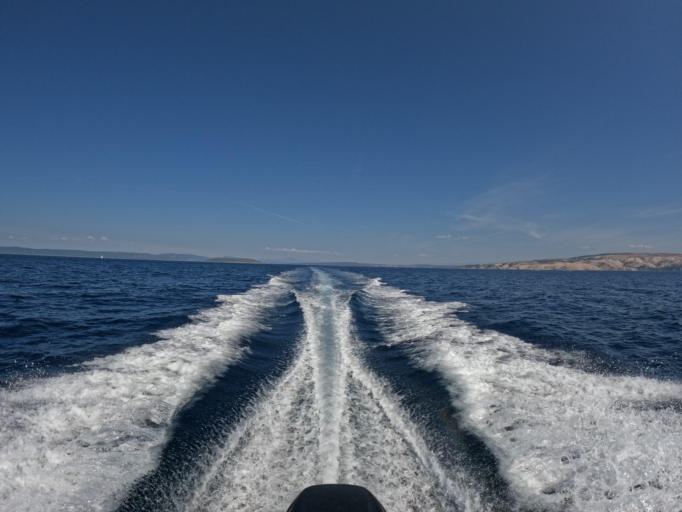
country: HR
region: Primorsko-Goranska
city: Punat
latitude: 44.9055
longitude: 14.6320
